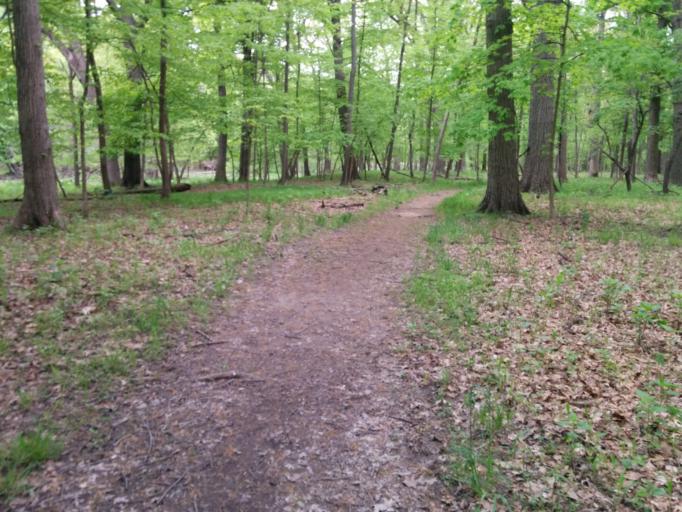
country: US
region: Illinois
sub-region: Cook County
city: Franklin Park
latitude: 41.9487
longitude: -87.8500
